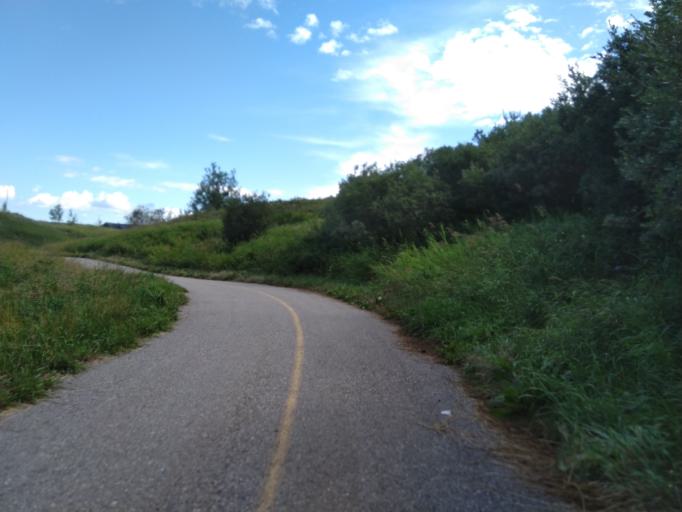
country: CA
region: Alberta
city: Calgary
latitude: 51.1622
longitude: -114.1354
